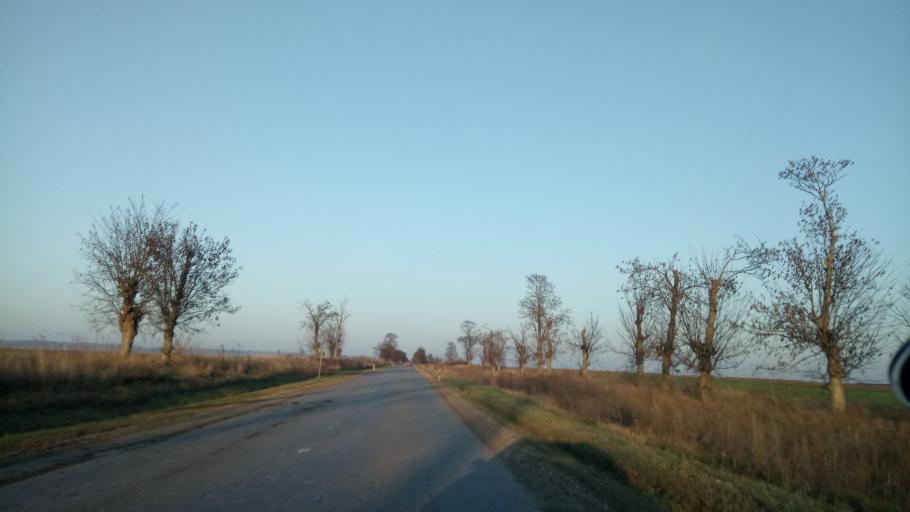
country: RS
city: Novi Karlovci
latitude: 45.0868
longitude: 20.1878
